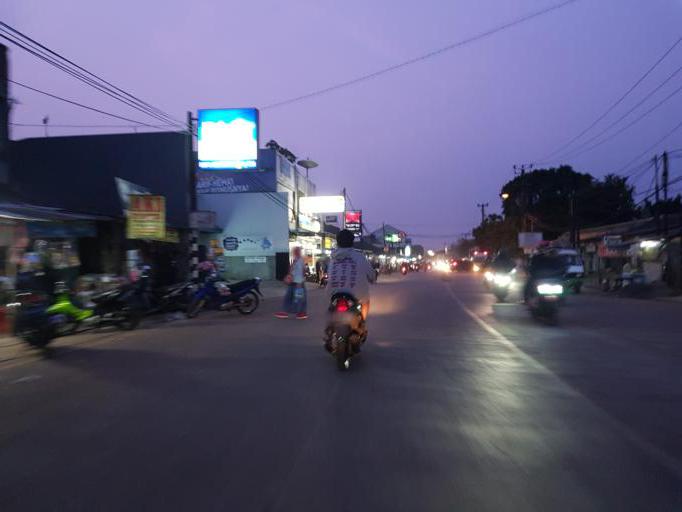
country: ID
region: West Java
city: Serpong
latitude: -6.3232
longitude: 106.6633
